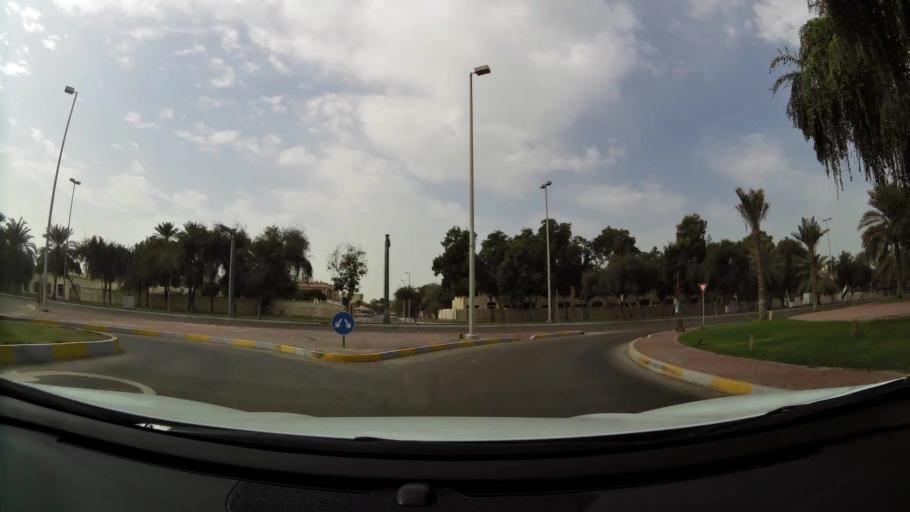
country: AE
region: Abu Dhabi
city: Abu Dhabi
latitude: 24.4441
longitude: 54.3732
